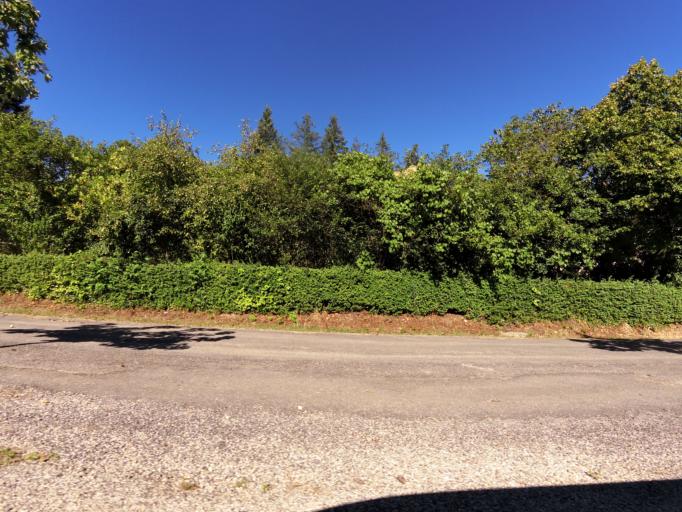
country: FR
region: Languedoc-Roussillon
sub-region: Departement du Gard
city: Saint-Jean-du-Gard
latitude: 44.1016
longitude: 3.8949
